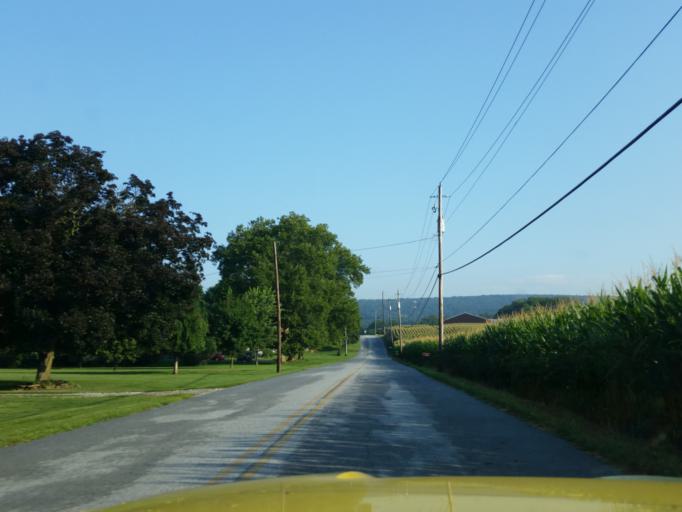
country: US
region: Pennsylvania
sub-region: York County
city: Stonybrook
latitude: 39.9918
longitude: -76.6275
